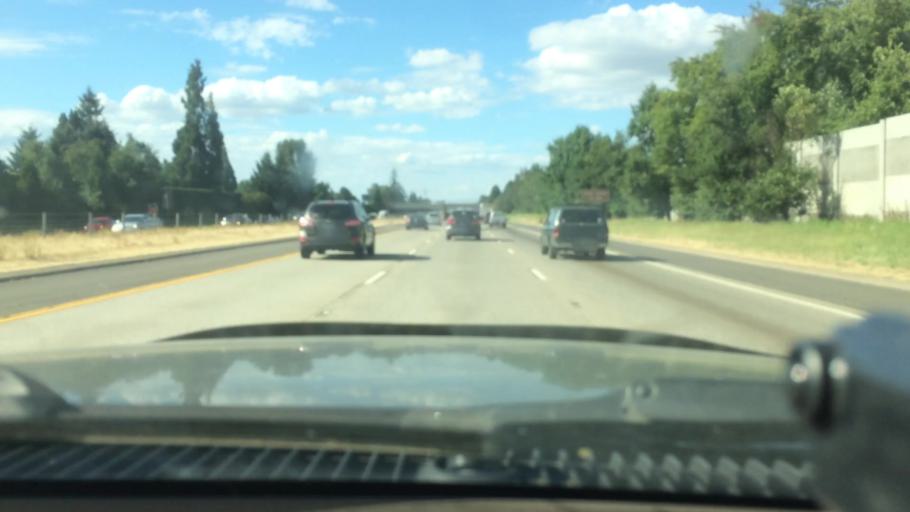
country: US
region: Oregon
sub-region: Marion County
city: Four Corners
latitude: 44.9353
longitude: -122.9902
